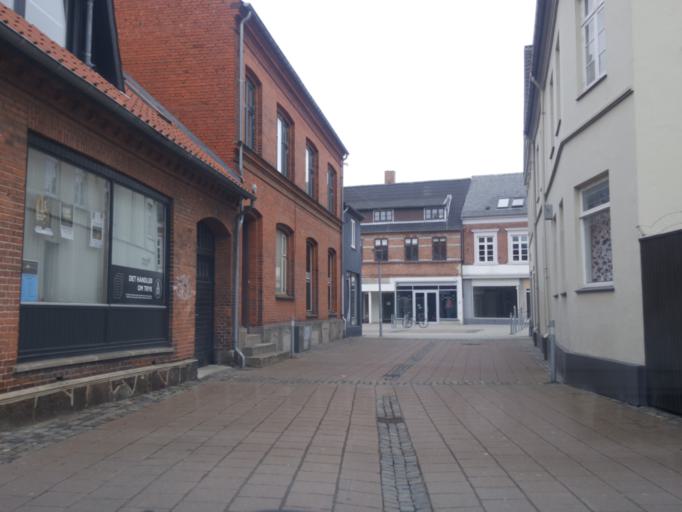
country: DK
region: Zealand
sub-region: Vordingborg Kommune
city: Vordingborg
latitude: 55.0094
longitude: 11.9067
